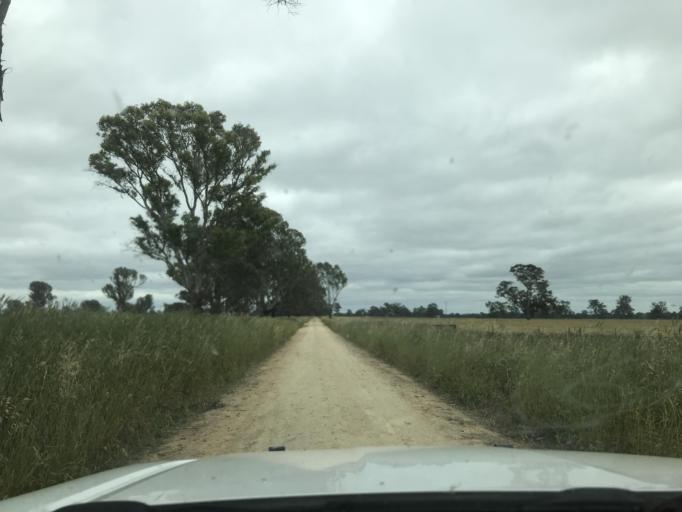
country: AU
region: South Australia
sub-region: Wattle Range
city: Penola
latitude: -37.1804
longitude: 141.0729
